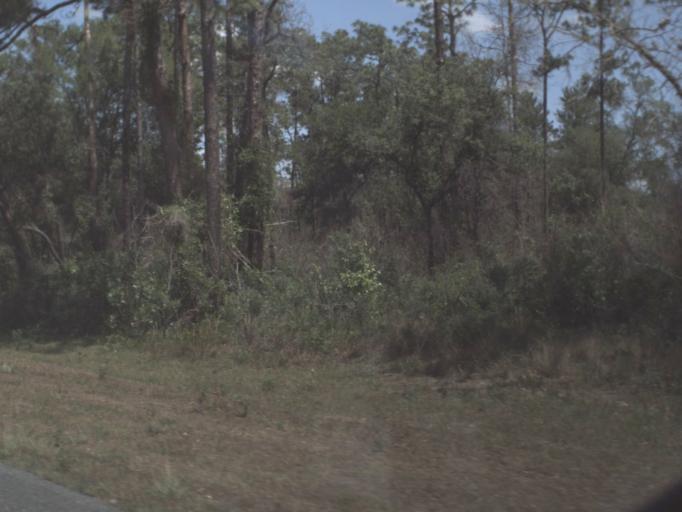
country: US
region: Florida
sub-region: Marion County
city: Silver Springs Shores
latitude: 29.2021
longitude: -81.9353
